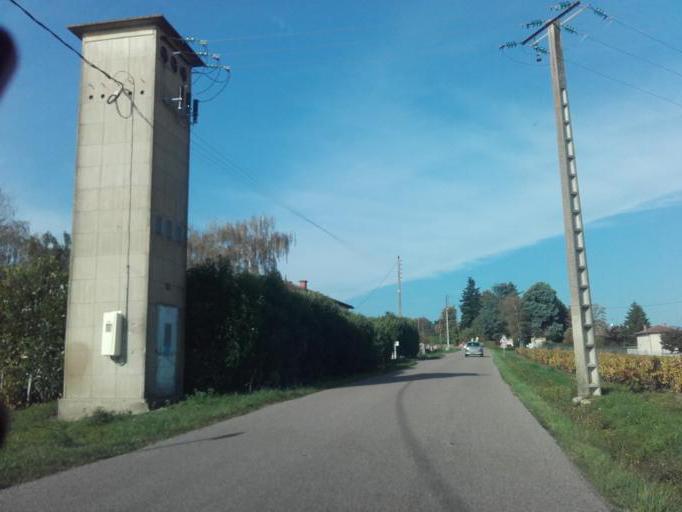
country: FR
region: Bourgogne
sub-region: Departement de Saone-et-Loire
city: La Chapelle-de-Guinchay
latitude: 46.2159
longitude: 4.7411
